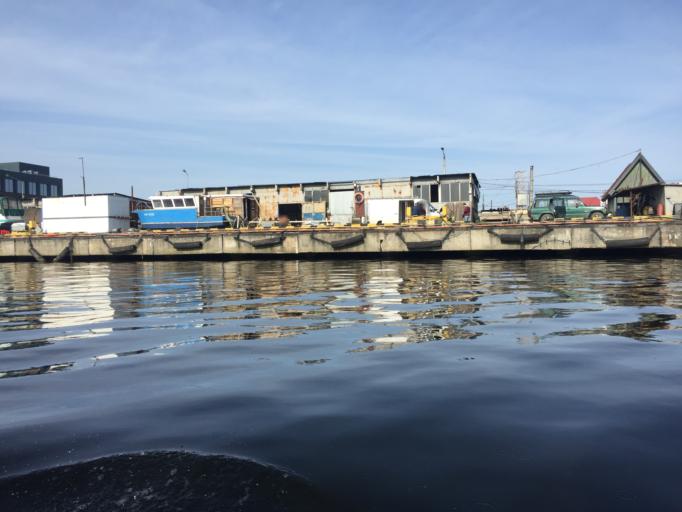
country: RU
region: Kaliningrad
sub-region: Gorod Kaliningrad
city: Kaliningrad
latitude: 54.7045
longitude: 20.4802
